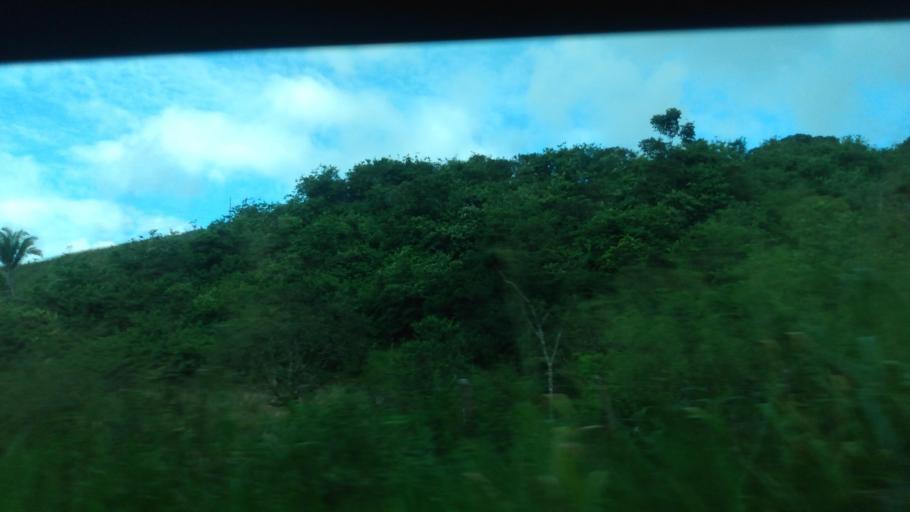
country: BR
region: Pernambuco
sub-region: Quipapa
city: Quipapa
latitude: -8.7891
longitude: -35.9784
